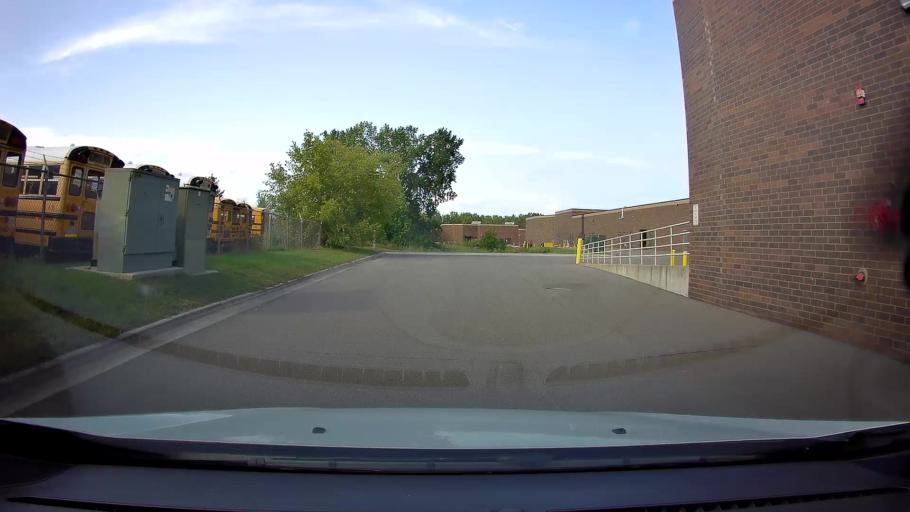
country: US
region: Minnesota
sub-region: Ramsey County
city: Roseville
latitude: 45.0232
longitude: -93.1711
